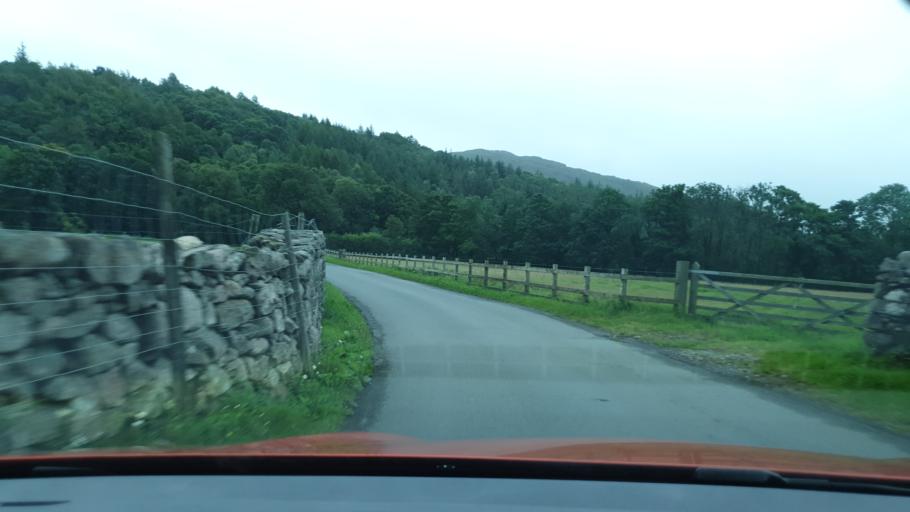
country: GB
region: England
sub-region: Cumbria
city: Seascale
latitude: 54.3855
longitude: -3.3122
